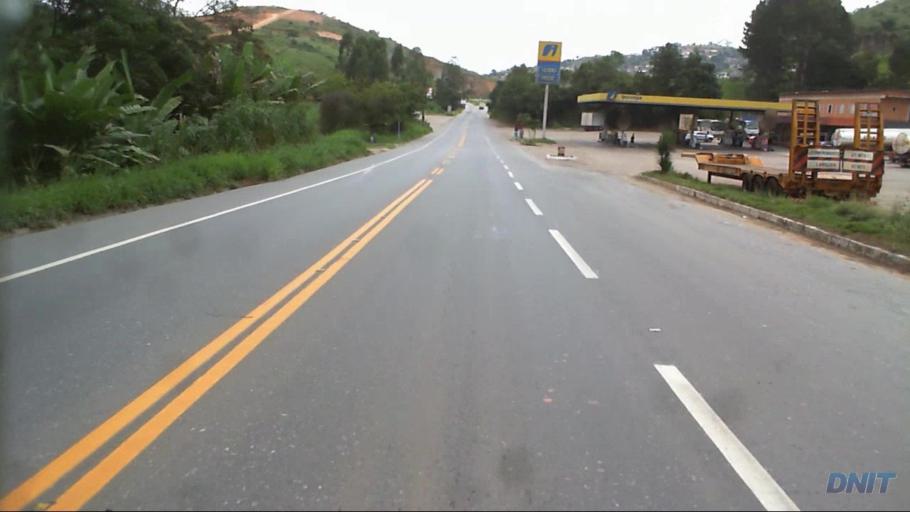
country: BR
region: Minas Gerais
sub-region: Nova Era
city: Nova Era
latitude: -19.7470
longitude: -43.0235
